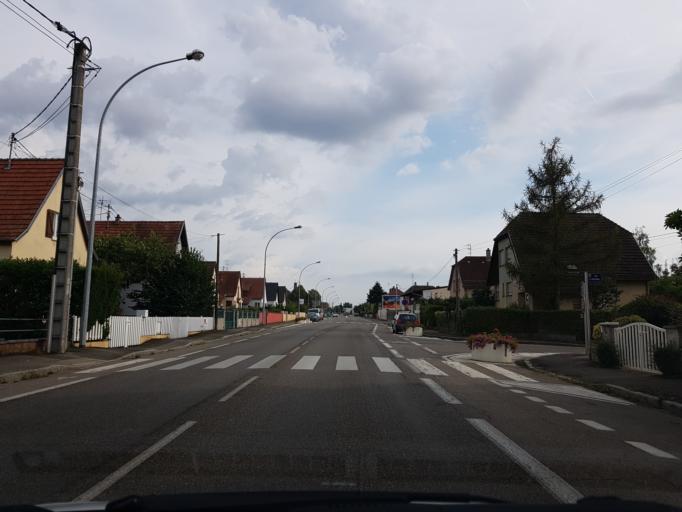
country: FR
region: Alsace
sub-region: Departement du Haut-Rhin
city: Wittenheim
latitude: 47.8211
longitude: 7.3398
